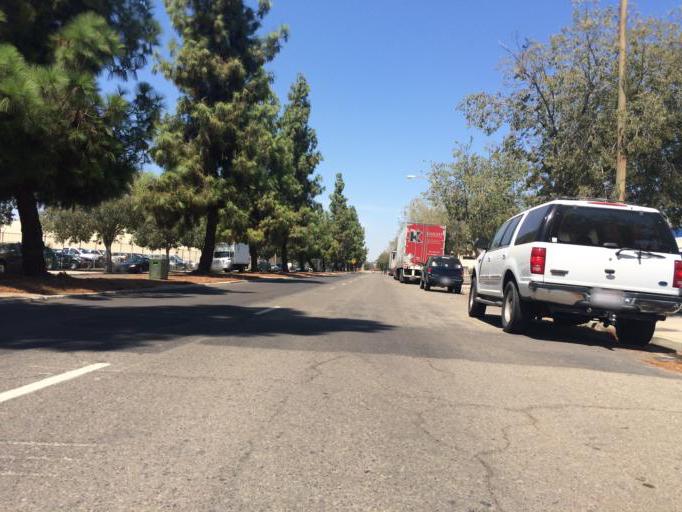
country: US
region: California
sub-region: Fresno County
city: Fresno
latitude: 36.7392
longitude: -119.8026
